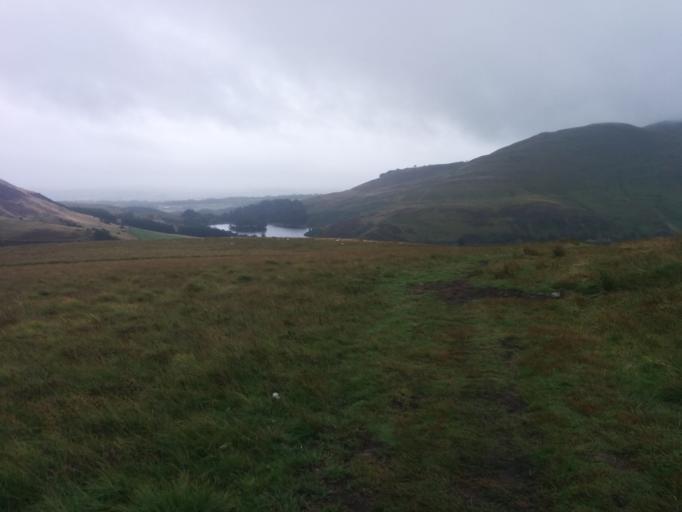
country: GB
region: Scotland
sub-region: Edinburgh
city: Colinton
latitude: 55.8680
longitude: -3.2582
